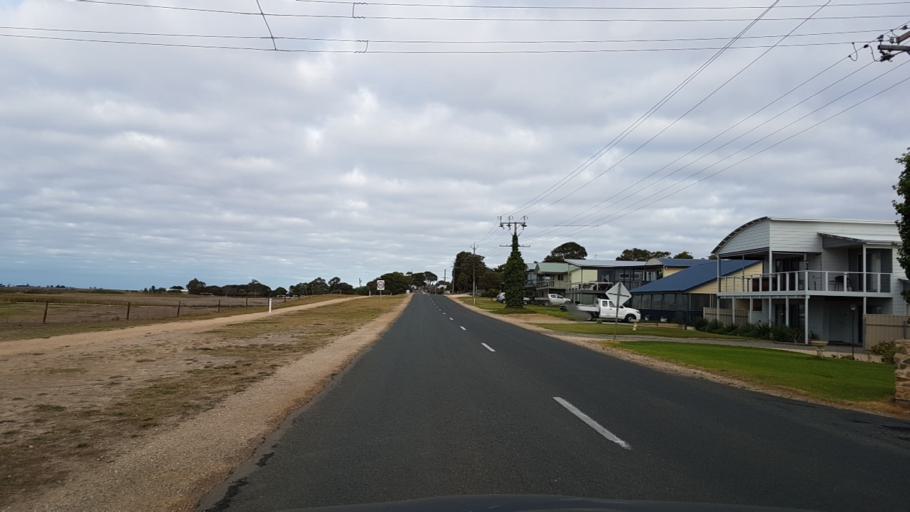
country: AU
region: South Australia
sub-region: Alexandrina
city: Langhorne Creek
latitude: -35.4027
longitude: 138.9806
